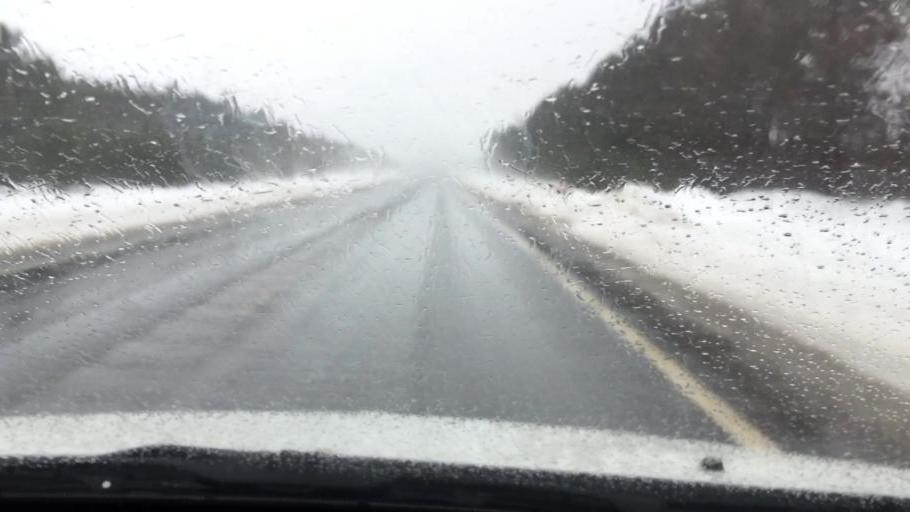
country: US
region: Michigan
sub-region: Antrim County
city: Mancelona
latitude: 44.9246
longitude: -85.0509
